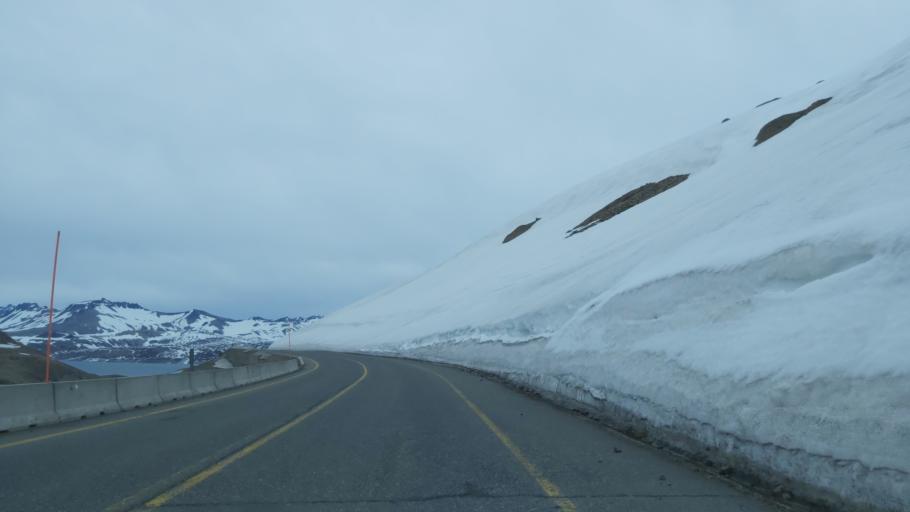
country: CL
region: Maule
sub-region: Provincia de Linares
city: Colbun
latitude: -36.0165
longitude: -70.4978
